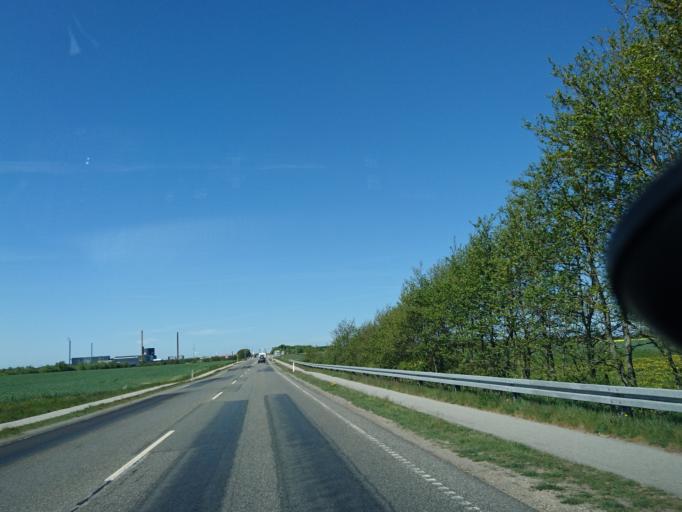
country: DK
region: North Denmark
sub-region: Hjorring Kommune
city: Hjorring
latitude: 57.4563
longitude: 10.0555
